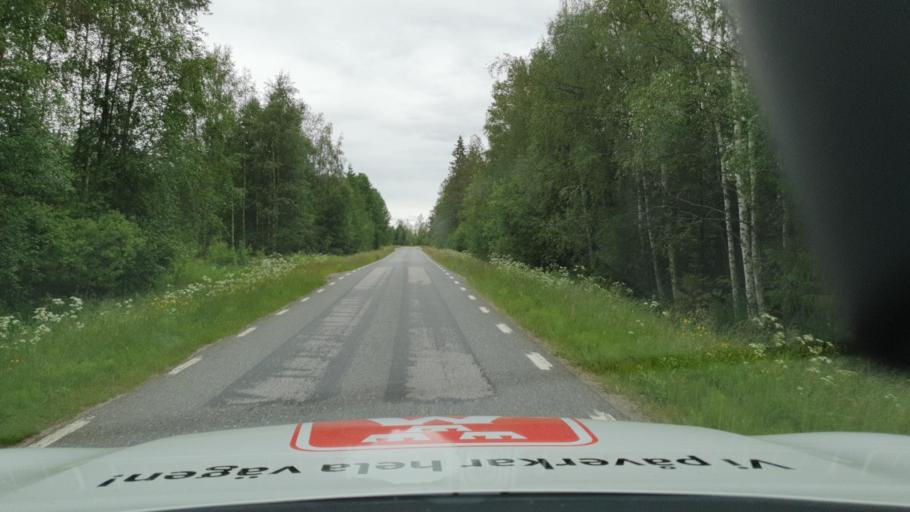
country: SE
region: Vaesterbotten
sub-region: Nordmalings Kommun
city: Nordmaling
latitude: 63.4932
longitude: 19.4359
